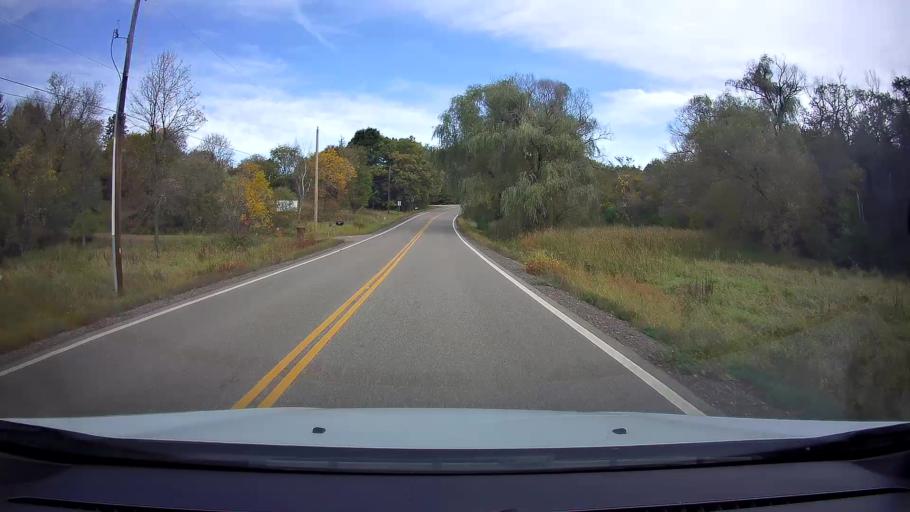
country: US
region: Minnesota
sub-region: Washington County
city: Stillwater
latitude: 45.0924
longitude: -92.8233
